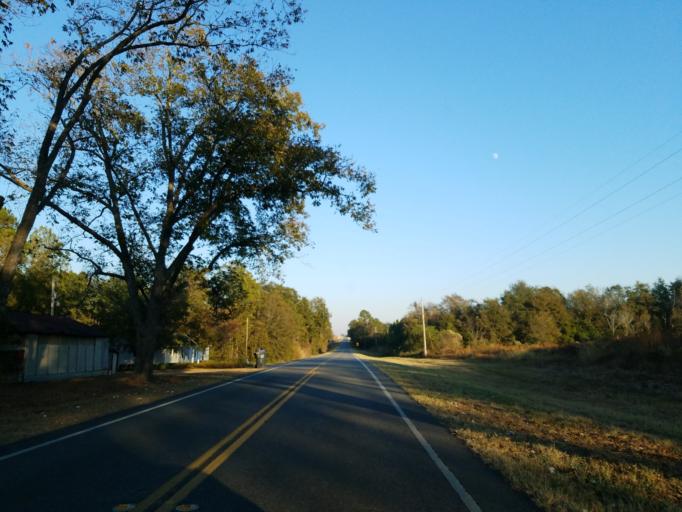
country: US
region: Georgia
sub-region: Turner County
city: Ashburn
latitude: 31.8595
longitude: -83.6172
